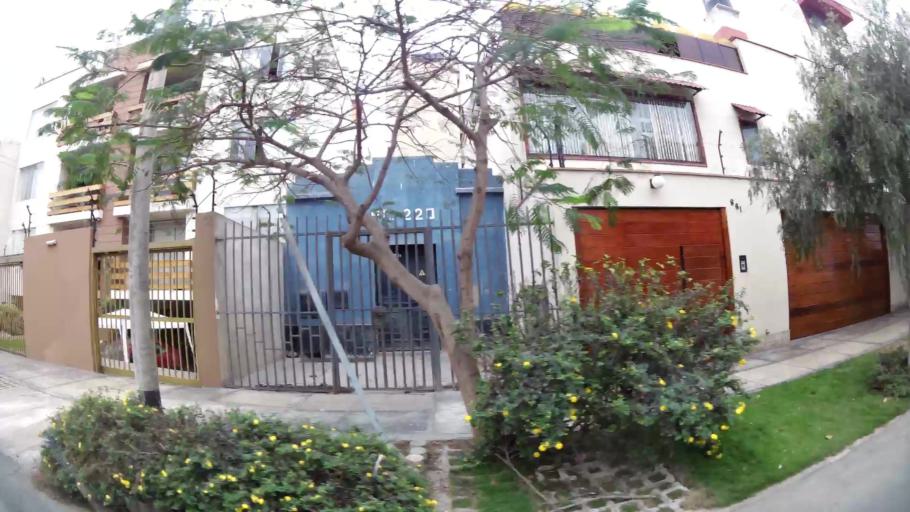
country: PE
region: Lima
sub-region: Lima
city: Surco
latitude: -12.1244
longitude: -77.0185
